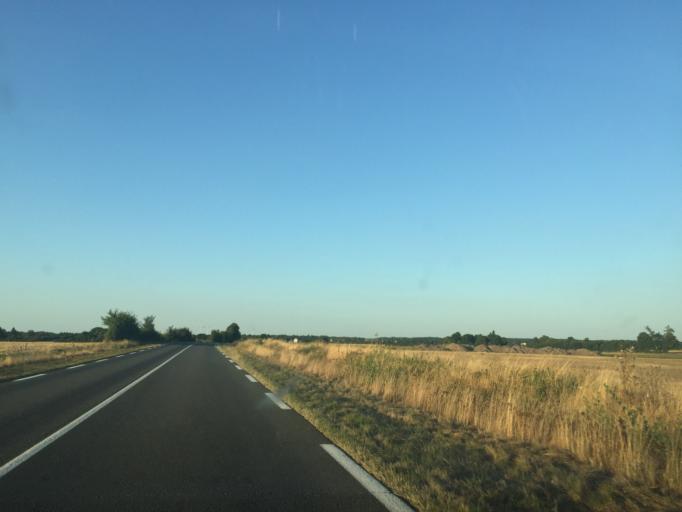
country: FR
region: Poitou-Charentes
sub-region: Departement de la Vienne
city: Saint-Sauvant
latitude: 46.3833
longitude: 0.0445
